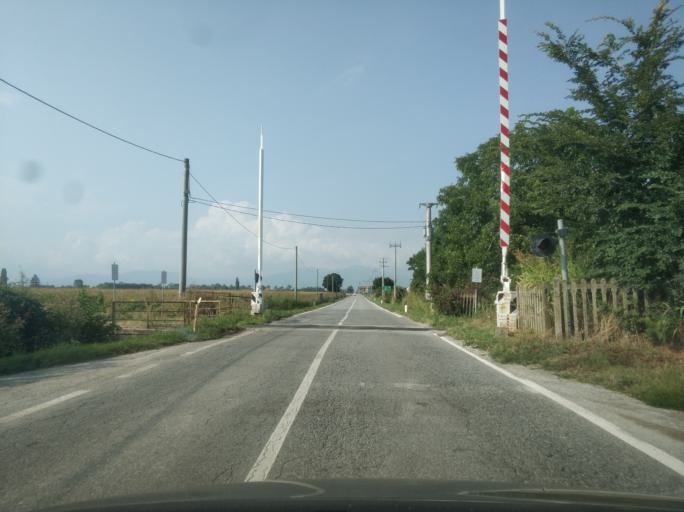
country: IT
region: Piedmont
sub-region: Provincia di Cuneo
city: Roata Rossi
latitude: 44.4742
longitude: 7.5156
